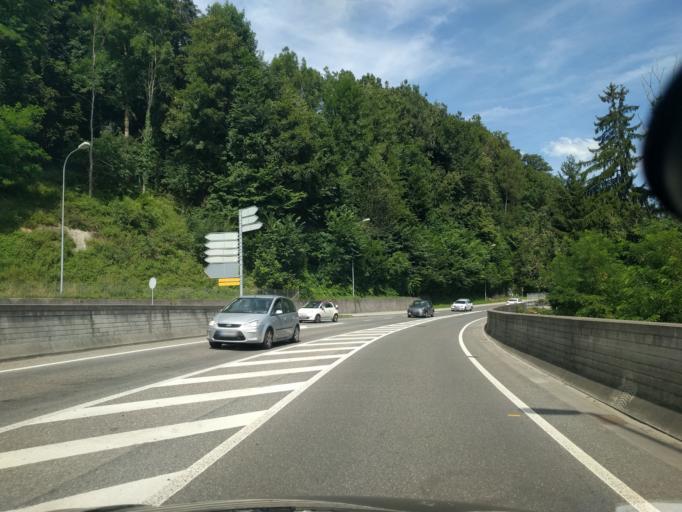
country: CH
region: Saint Gallen
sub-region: Wahlkreis See-Gaster
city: Schmerikon
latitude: 47.2435
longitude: 8.9490
